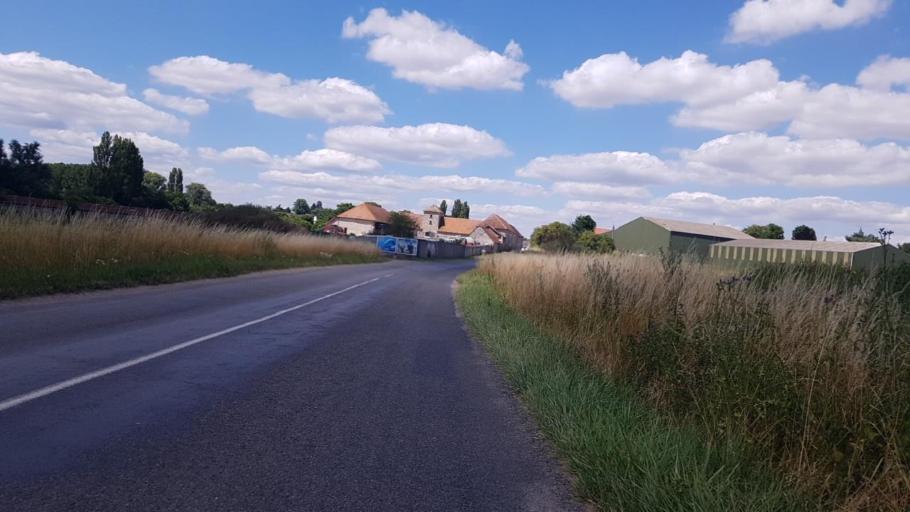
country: FR
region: Ile-de-France
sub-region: Departement de Seine-et-Marne
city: Juilly
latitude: 49.0038
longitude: 2.6687
